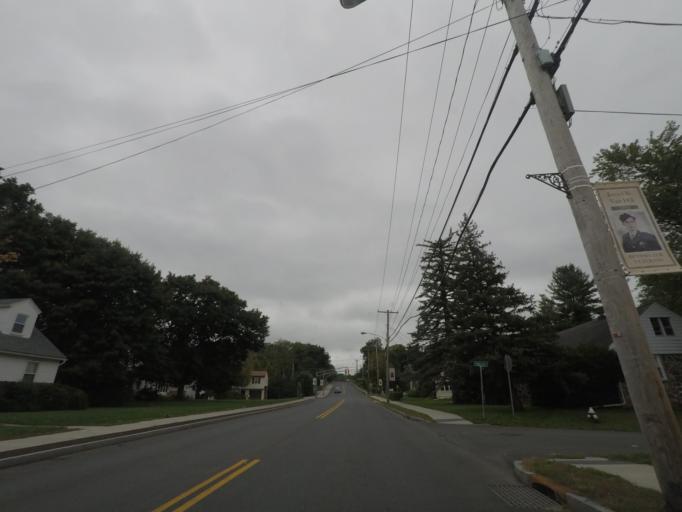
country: US
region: New York
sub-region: Rensselaer County
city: Rensselaer
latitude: 42.6548
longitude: -73.7051
